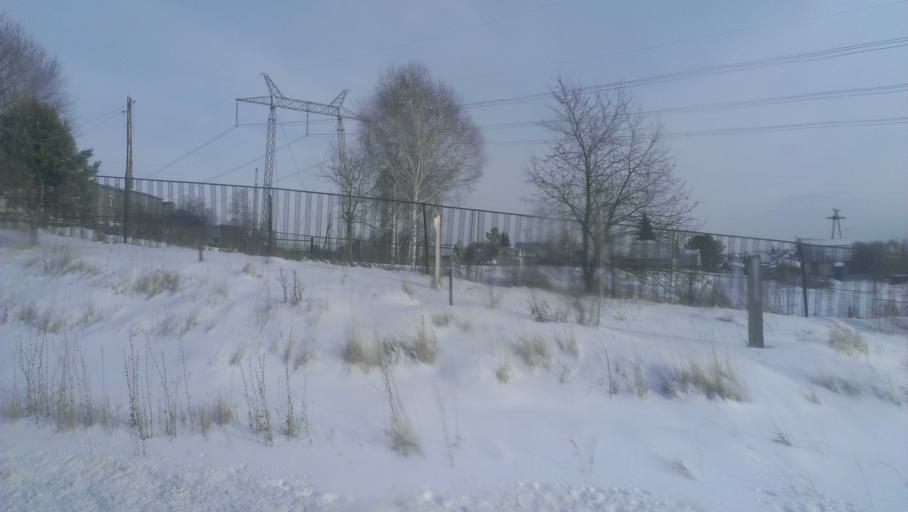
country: RU
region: Altai Krai
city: Gon'ba
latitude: 53.4163
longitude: 83.5500
